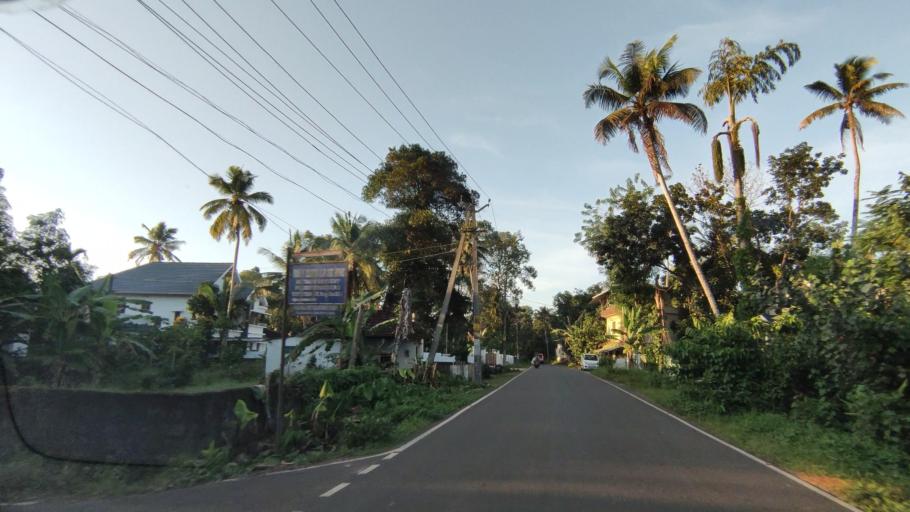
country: IN
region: Kerala
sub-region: Kottayam
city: Kottayam
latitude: 9.6247
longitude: 76.4915
